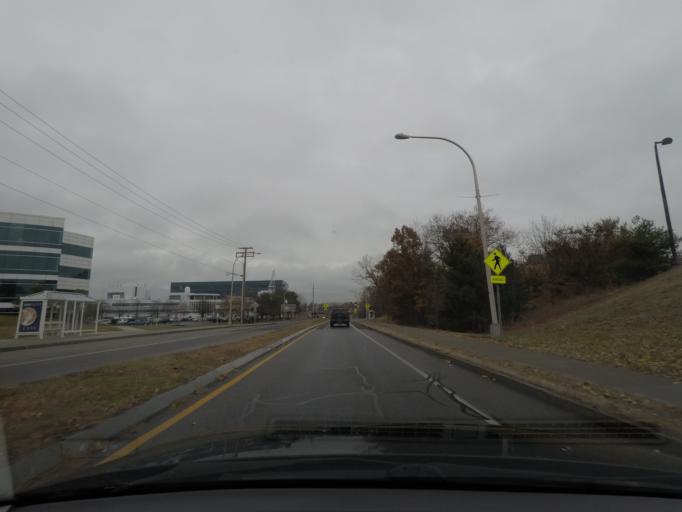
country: US
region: New York
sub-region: Albany County
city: McKownville
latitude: 42.6899
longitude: -73.8306
